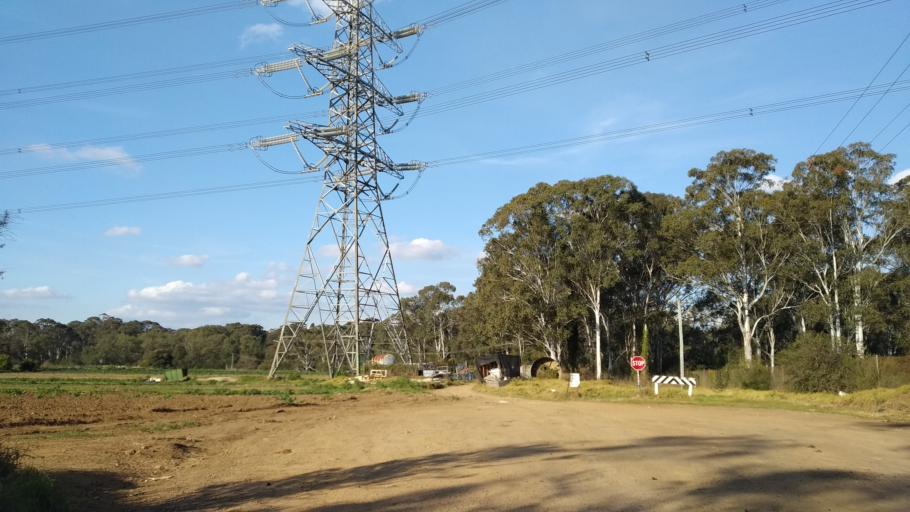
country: AU
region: New South Wales
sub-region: Penrith Municipality
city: Werrington County
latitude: -33.7181
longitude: 150.7627
